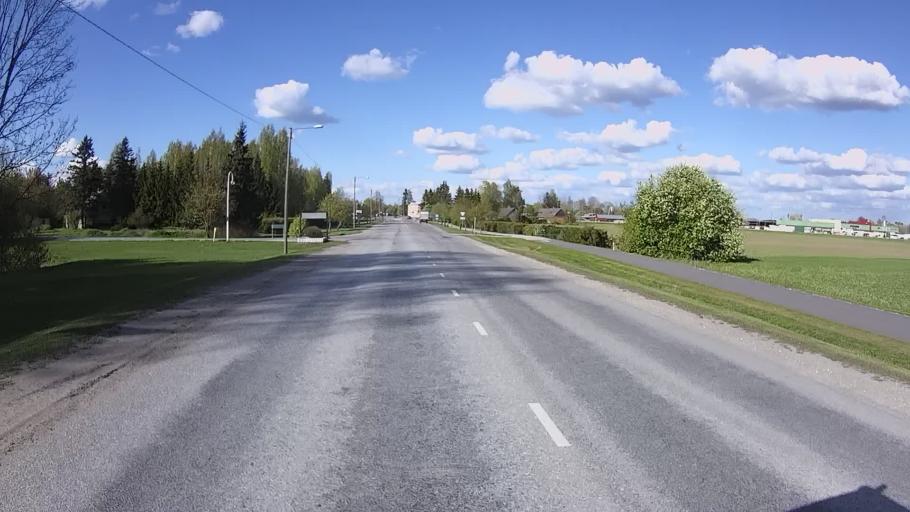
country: EE
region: Jogevamaa
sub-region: Poltsamaa linn
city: Poltsamaa
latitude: 58.6608
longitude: 25.9878
